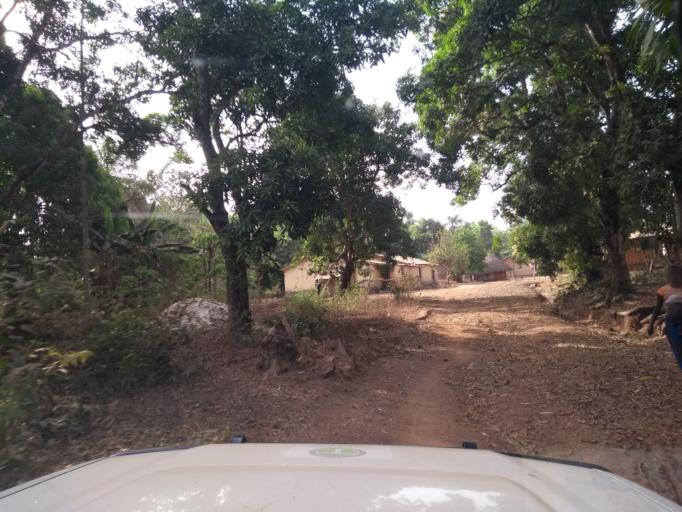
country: GN
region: Kindia
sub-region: Prefecture de Dubreka
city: Dubreka
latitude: 9.8334
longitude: -13.5575
